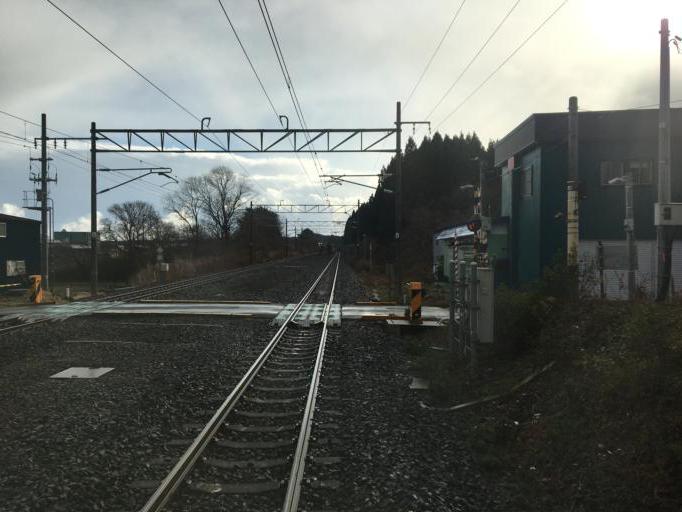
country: JP
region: Aomori
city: Aomori Shi
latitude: 40.9201
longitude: 141.0275
